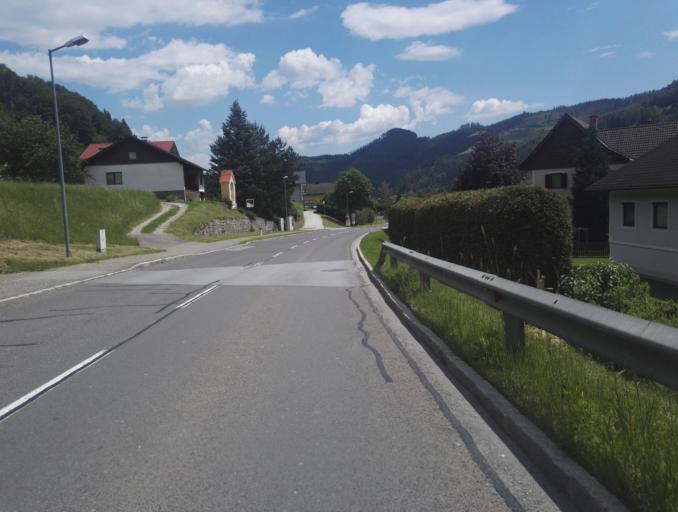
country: AT
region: Styria
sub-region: Politischer Bezirk Graz-Umgebung
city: Ubelbach
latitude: 47.2204
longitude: 15.2519
